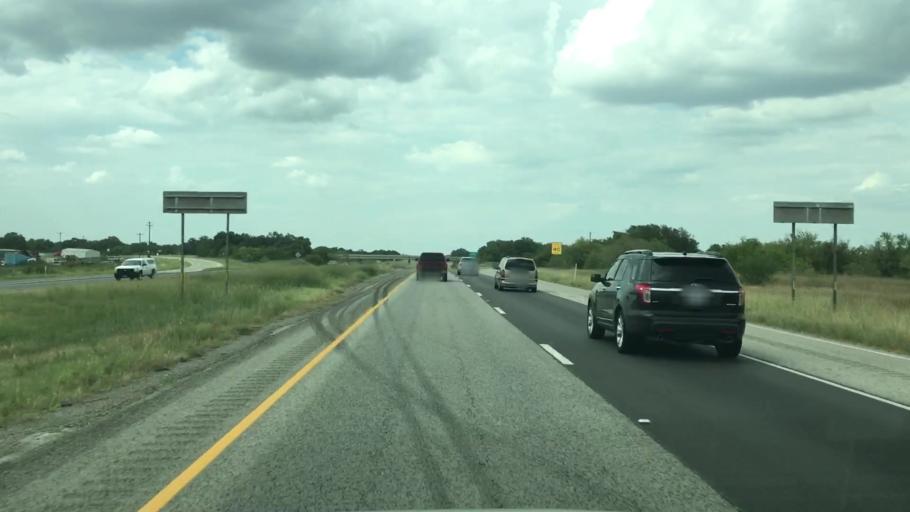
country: US
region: Texas
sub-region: Atascosa County
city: Pleasanton
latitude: 29.0469
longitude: -98.4316
